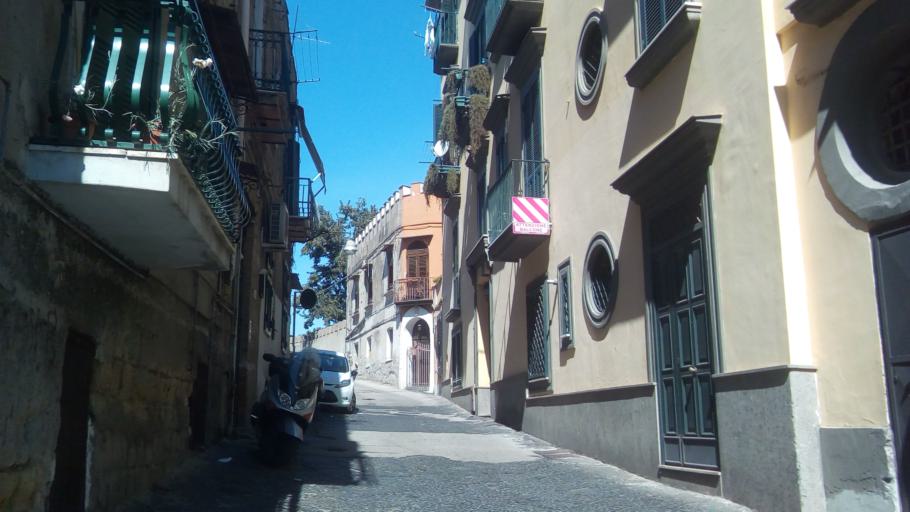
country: IT
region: Campania
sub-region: Provincia di Napoli
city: Napoli
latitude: 40.8641
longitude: 14.2577
